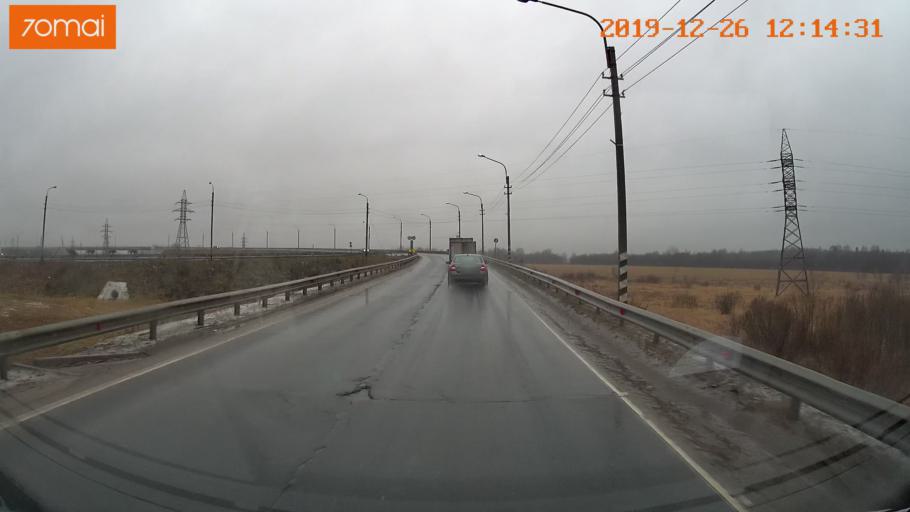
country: RU
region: Vologda
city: Tonshalovo
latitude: 59.2134
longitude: 37.9388
